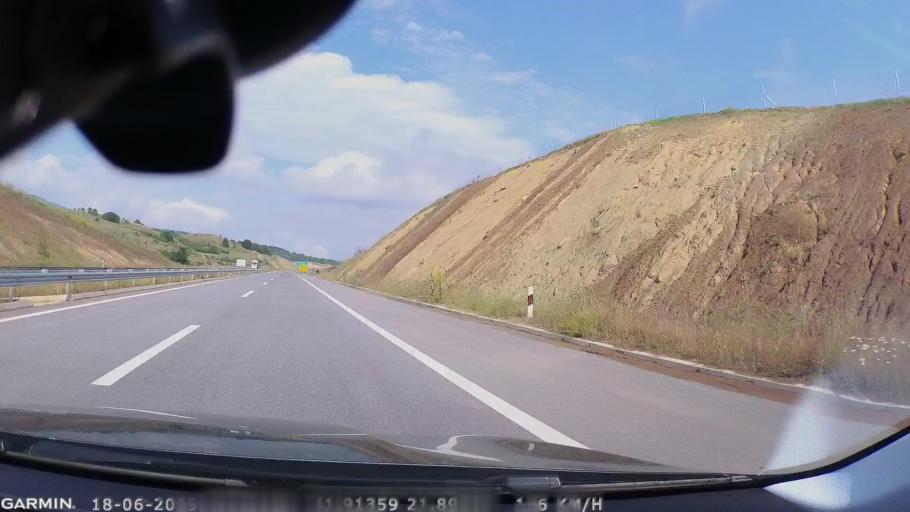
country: MK
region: Sveti Nikole
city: Gorobinci
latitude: 41.9132
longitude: 21.8931
